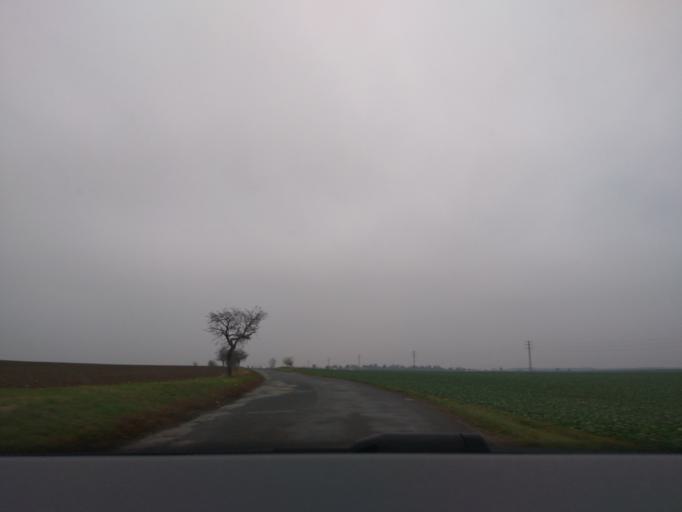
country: CZ
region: Praha
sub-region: Praha 19
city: Kbely
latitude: 50.1672
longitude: 14.5616
